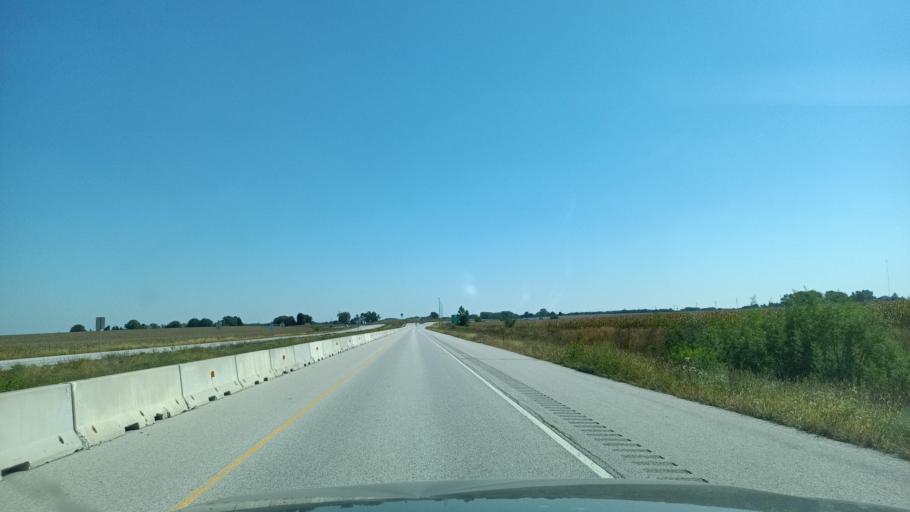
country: US
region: Illinois
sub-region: McDonough County
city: Macomb
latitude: 40.5032
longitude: -90.6849
